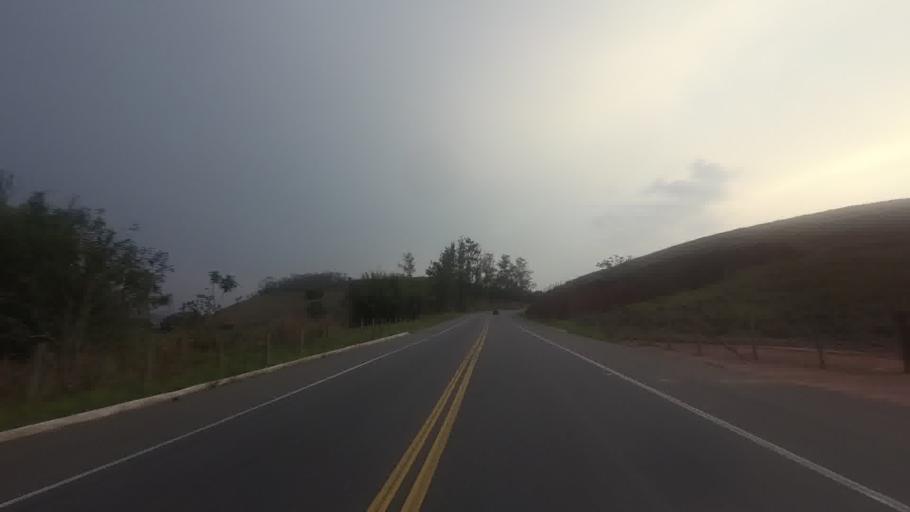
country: BR
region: Rio de Janeiro
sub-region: Carmo
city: Carmo
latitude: -21.8018
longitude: -42.5728
